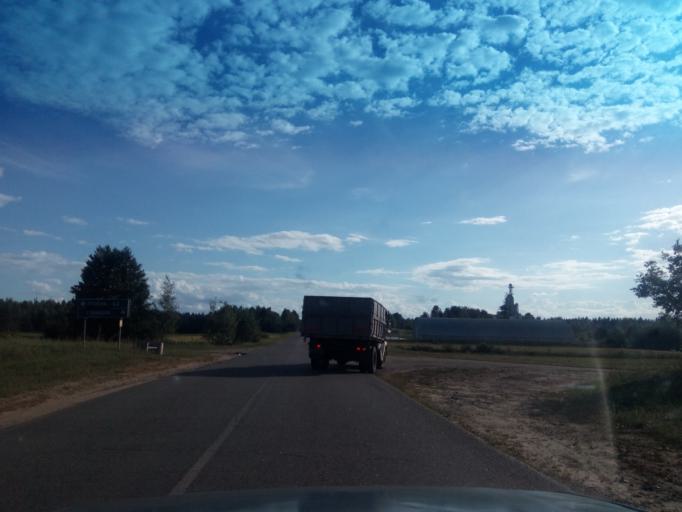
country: BY
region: Vitebsk
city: Polatsk
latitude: 55.4346
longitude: 28.7726
